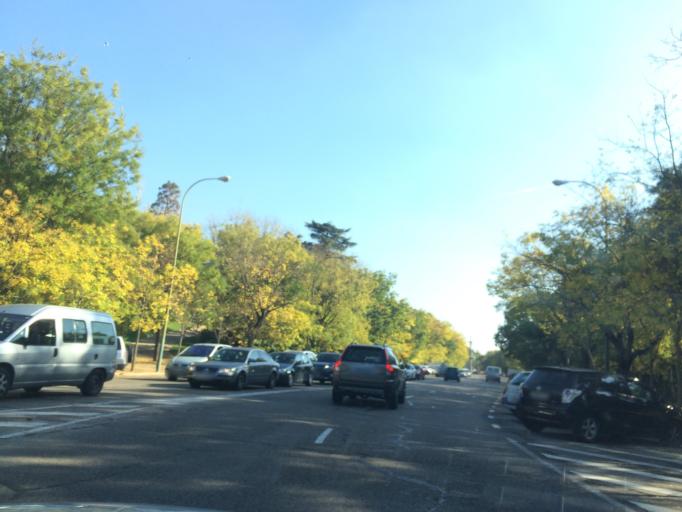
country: ES
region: Madrid
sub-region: Provincia de Madrid
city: Moncloa-Aravaca
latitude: 40.4326
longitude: -3.7272
